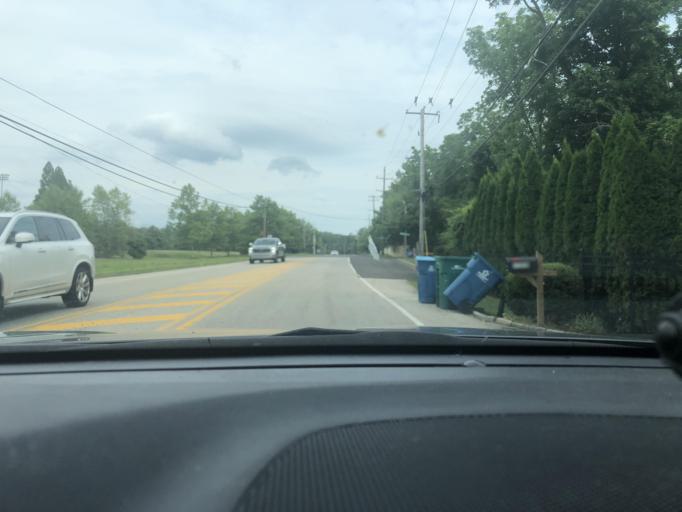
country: US
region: Pennsylvania
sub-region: Montgomery County
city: Spring House
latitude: 40.1943
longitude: -75.2429
